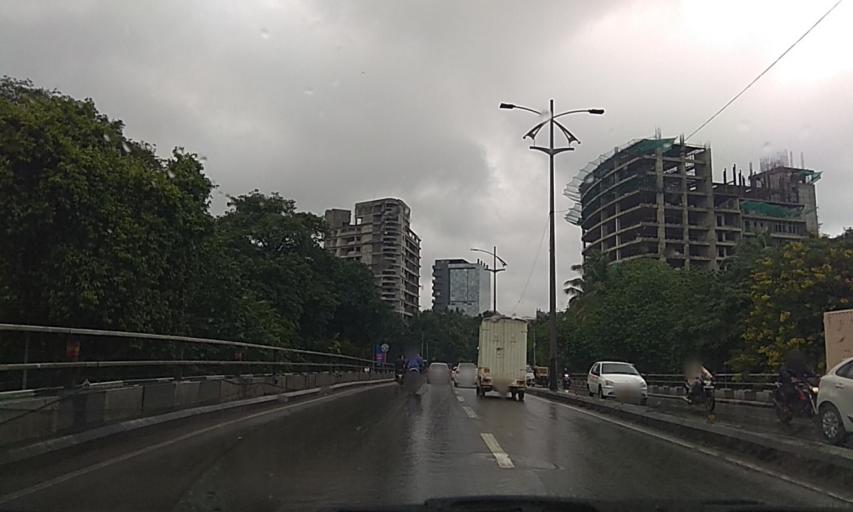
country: IN
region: Maharashtra
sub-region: Pune Division
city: Shivaji Nagar
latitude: 18.5314
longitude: 73.8446
